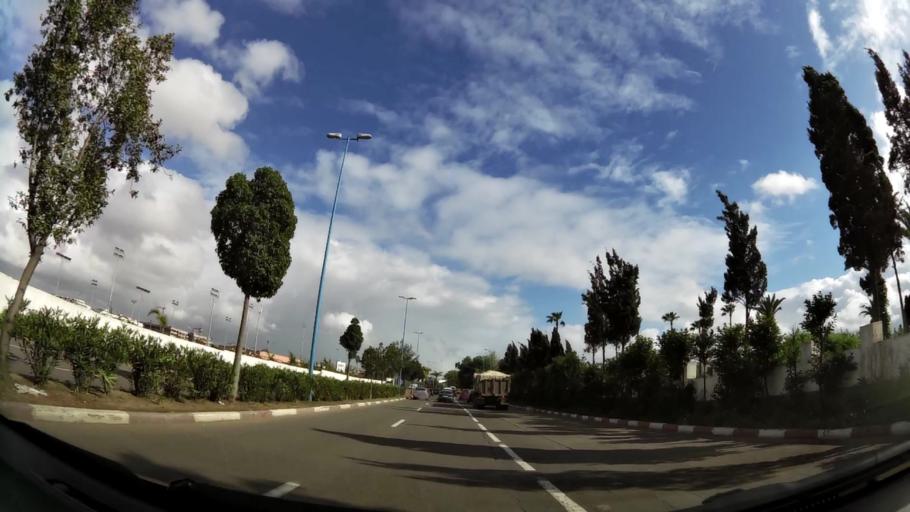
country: MA
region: Grand Casablanca
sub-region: Casablanca
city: Casablanca
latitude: 33.5437
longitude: -7.6201
